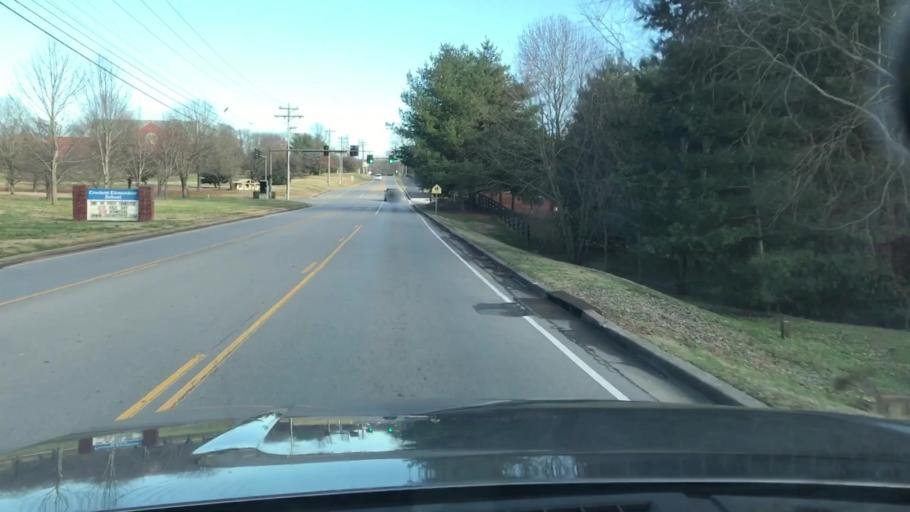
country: US
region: Tennessee
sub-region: Williamson County
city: Brentwood Estates
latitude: 35.9772
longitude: -86.7727
